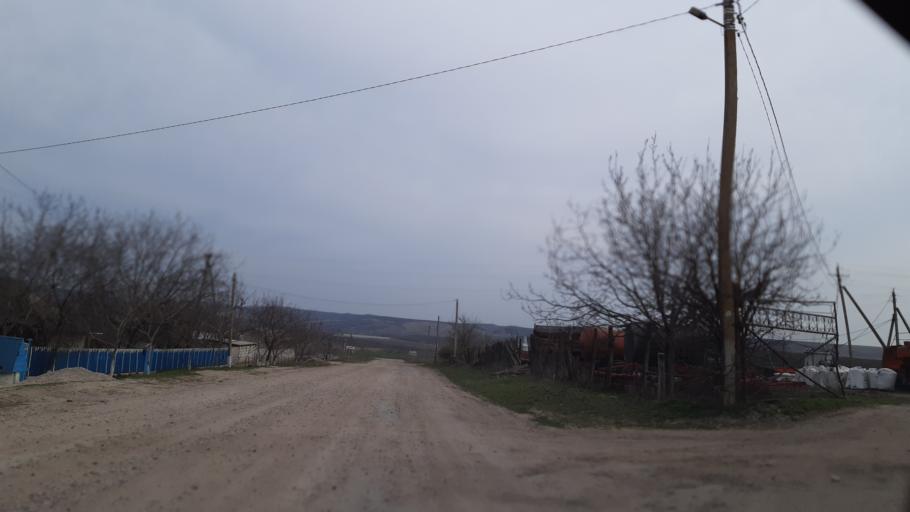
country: MD
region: Soldanesti
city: Soldanesti
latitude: 47.7094
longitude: 28.7088
